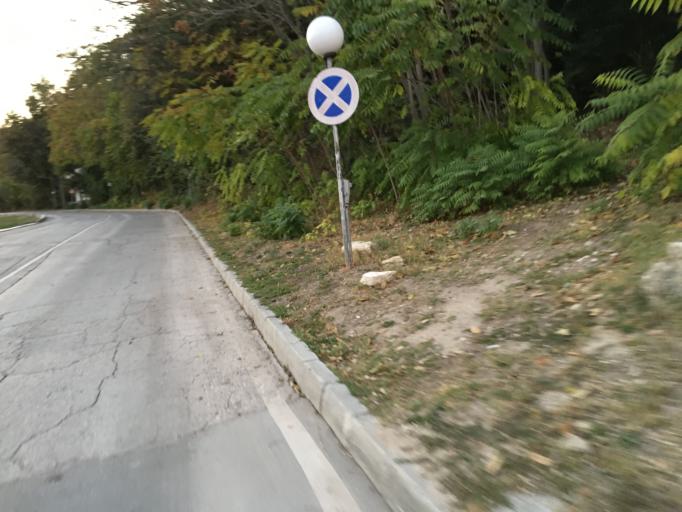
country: BG
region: Dobrich
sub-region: Obshtina Balchik
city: Balchik
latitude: 43.3731
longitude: 28.0879
